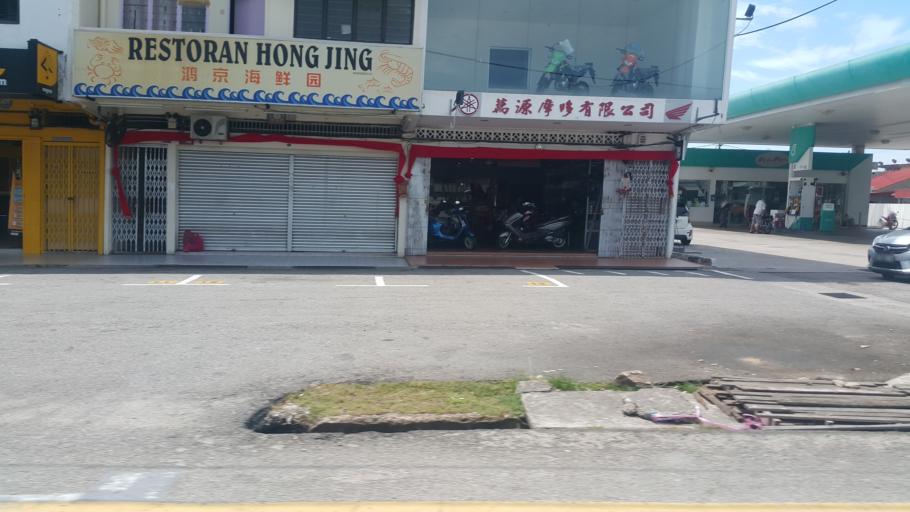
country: MY
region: Melaka
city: Kampung Bukit Baharu
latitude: 2.1871
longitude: 102.2712
